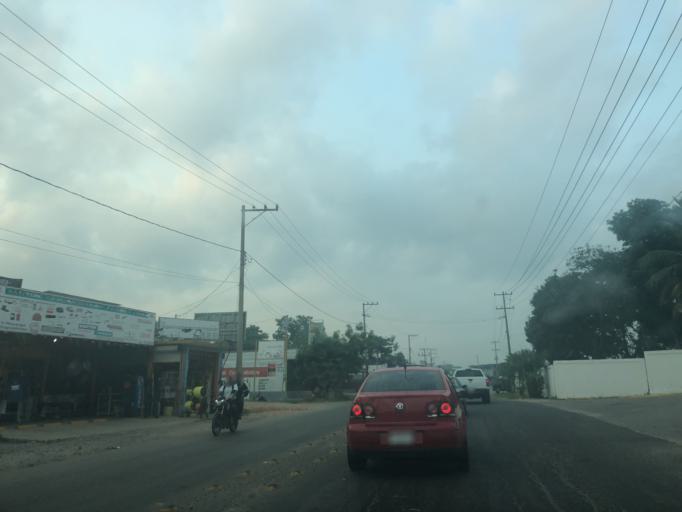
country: MX
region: Chiapas
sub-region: Reforma
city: El Carmen (El Limon)
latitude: 17.8701
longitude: -93.1534
